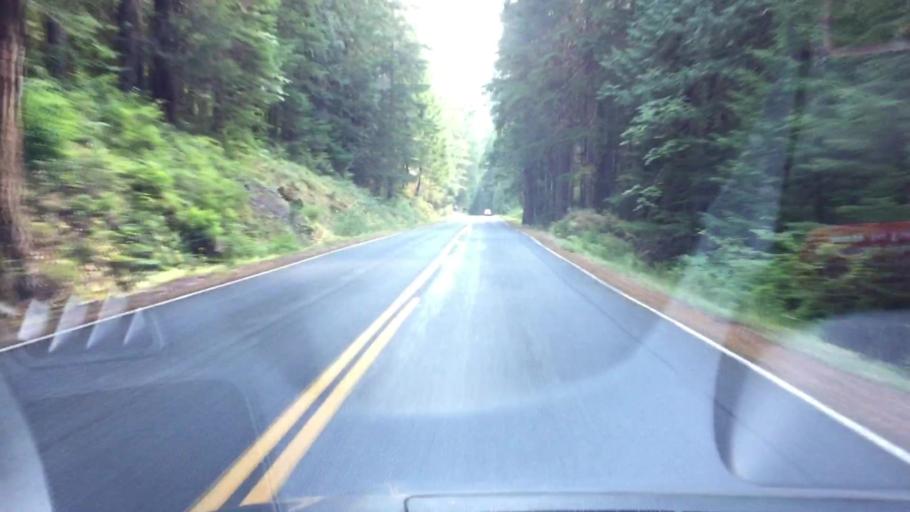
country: US
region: Washington
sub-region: Pierce County
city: Buckley
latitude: 46.7226
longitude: -121.5756
